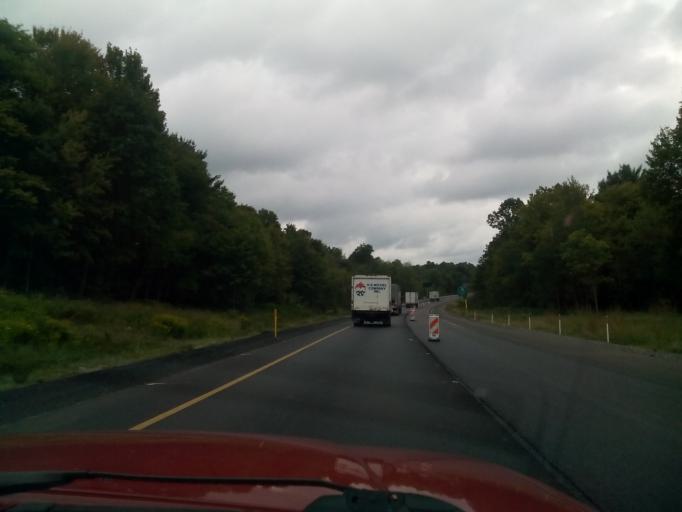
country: US
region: Pennsylvania
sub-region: Jefferson County
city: Falls Creek
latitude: 41.1576
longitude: -78.8302
